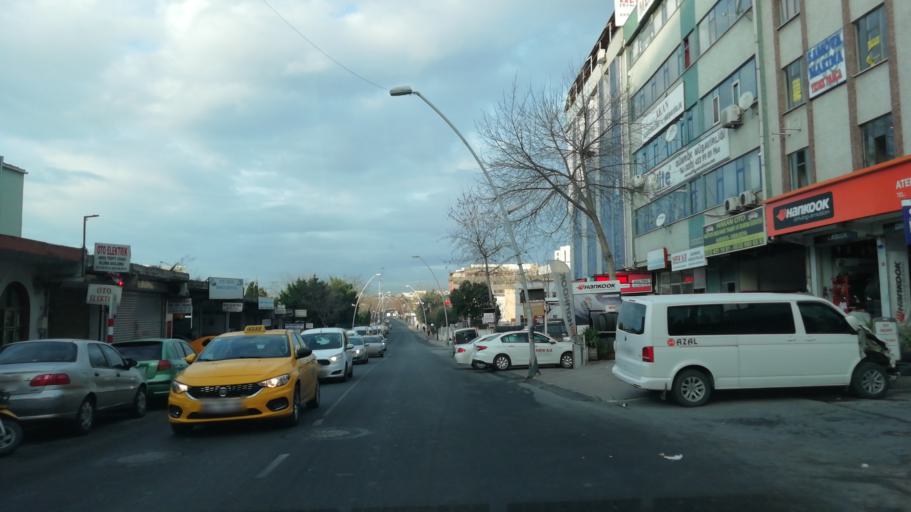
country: TR
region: Istanbul
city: Bahcelievler
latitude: 41.0009
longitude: 28.8267
